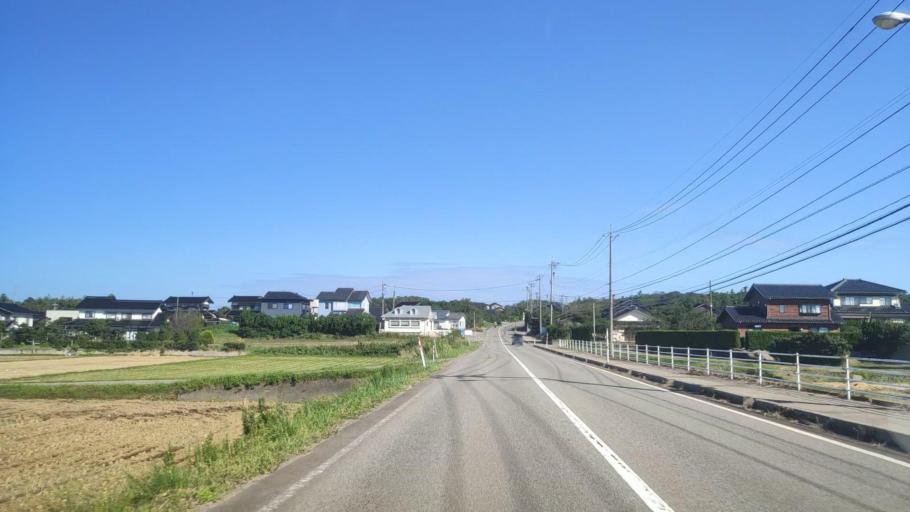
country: JP
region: Ishikawa
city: Hakui
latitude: 36.9833
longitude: 136.7760
